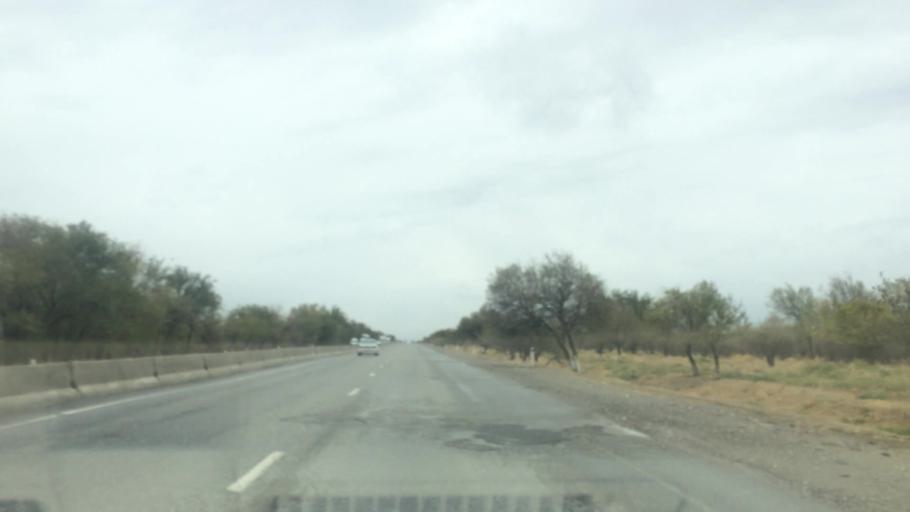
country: UZ
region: Samarqand
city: Bulung'ur
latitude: 39.8224
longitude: 67.3932
